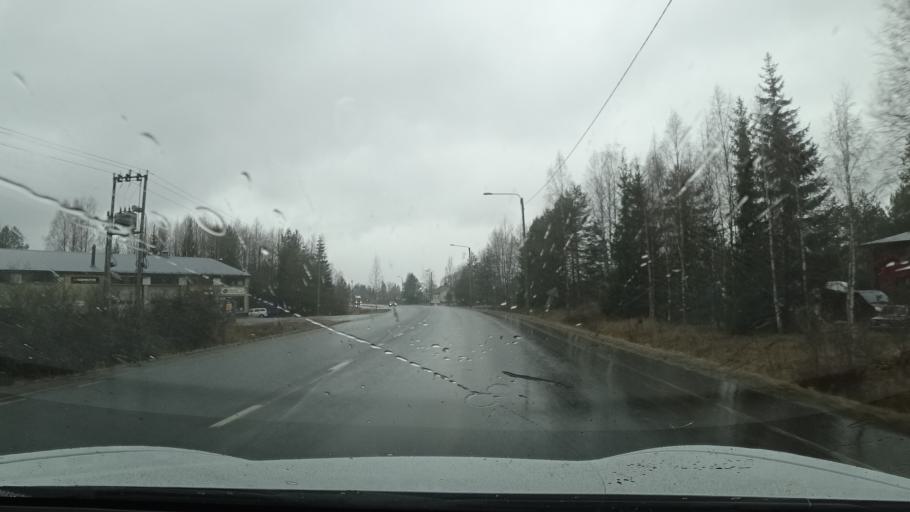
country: FI
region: Paijanne Tavastia
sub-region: Lahti
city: Orimattila
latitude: 60.8023
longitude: 25.7674
